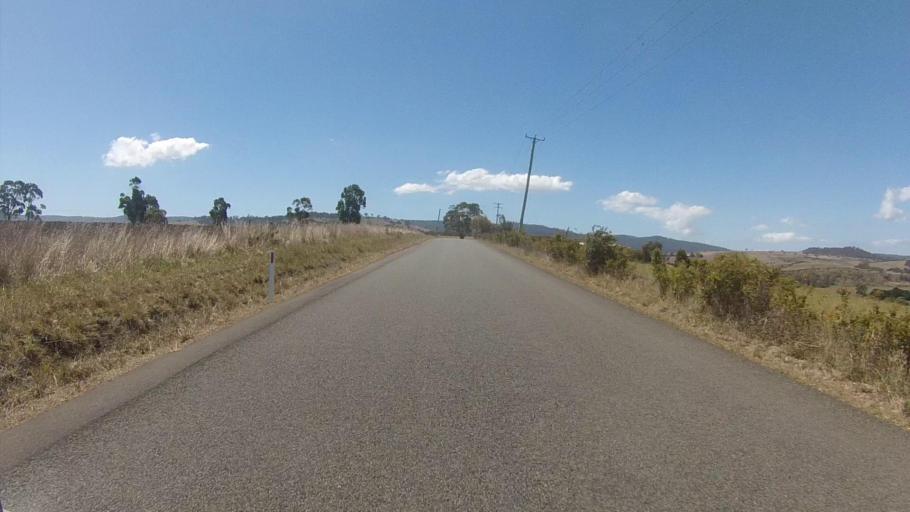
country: AU
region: Tasmania
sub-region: Sorell
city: Sorell
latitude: -42.7749
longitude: 147.5809
